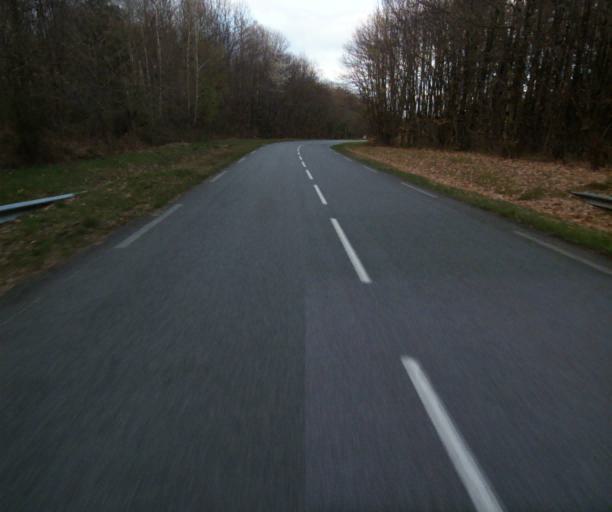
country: FR
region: Limousin
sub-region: Departement de la Correze
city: Correze
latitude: 45.2864
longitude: 1.8611
